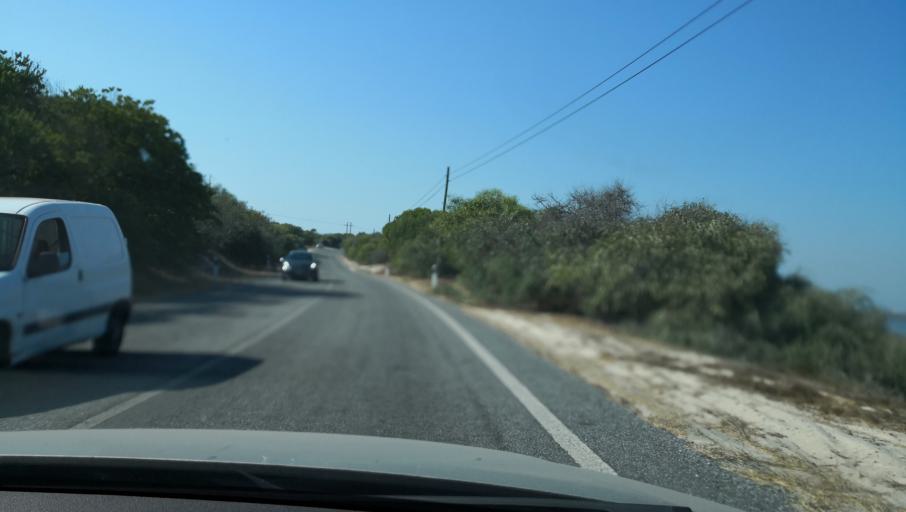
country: PT
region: Setubal
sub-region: Setubal
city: Setubal
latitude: 38.4181
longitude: -8.8173
